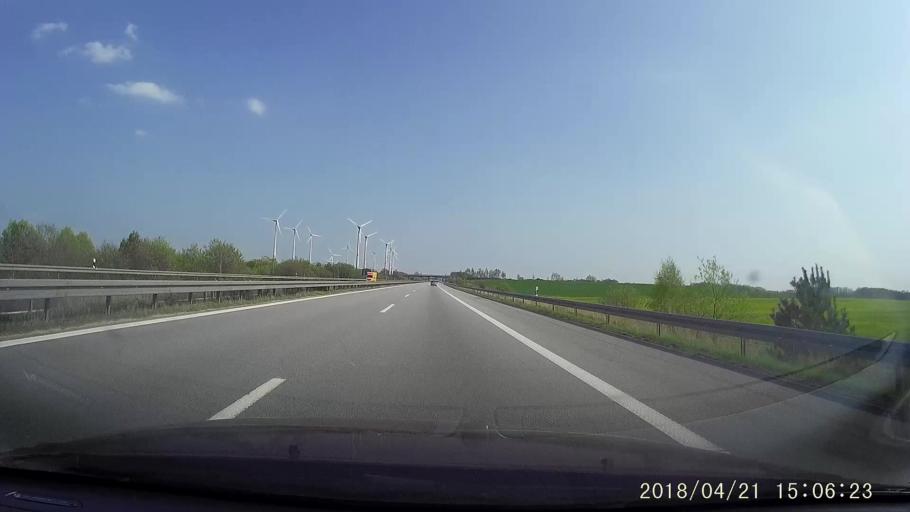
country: DE
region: Saxony
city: Kodersdorf
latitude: 51.2144
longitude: 14.9342
